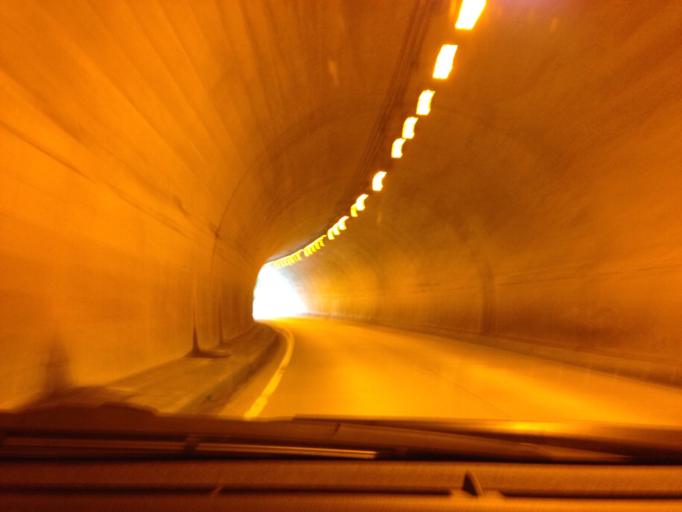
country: JP
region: Toyama
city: Fukumitsu
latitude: 36.5631
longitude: 136.7779
